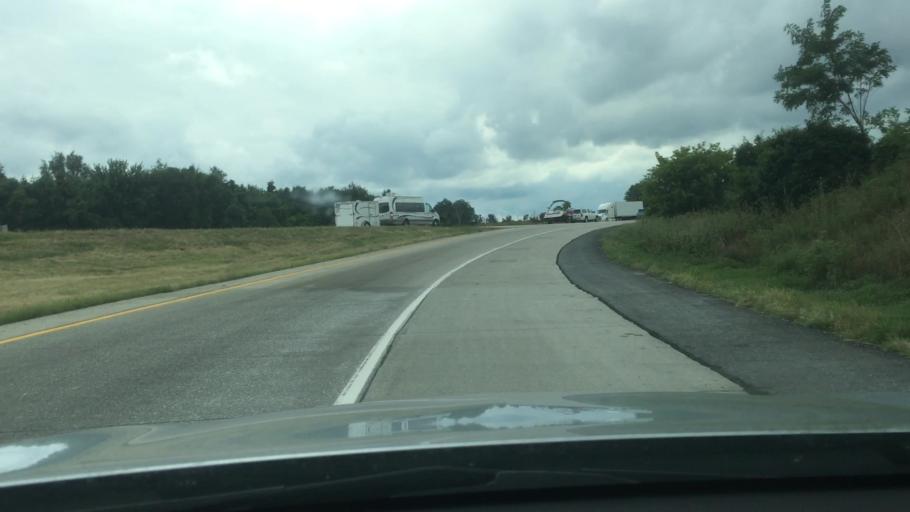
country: US
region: Pennsylvania
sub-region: Cumberland County
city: Schlusser
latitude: 40.2335
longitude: -77.1298
